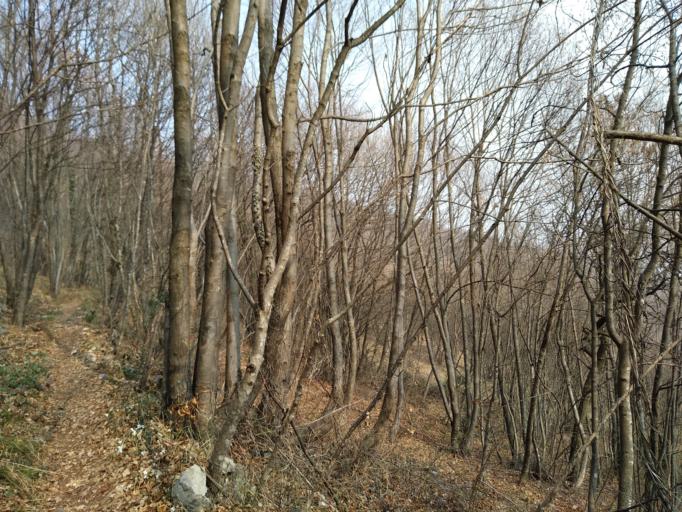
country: IT
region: Veneto
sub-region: Provincia di Vicenza
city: Santorso
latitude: 45.7471
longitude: 11.4039
